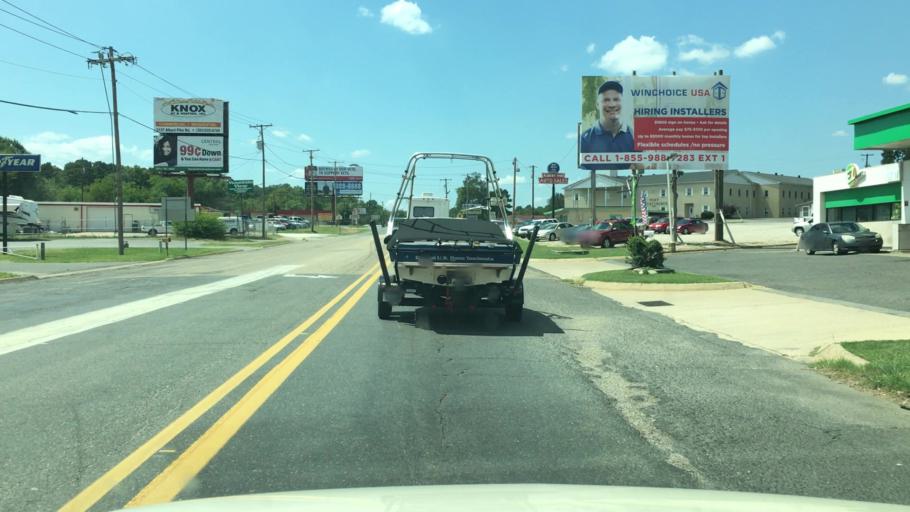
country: US
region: Arkansas
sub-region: Garland County
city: Piney
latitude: 34.5038
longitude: -93.1264
